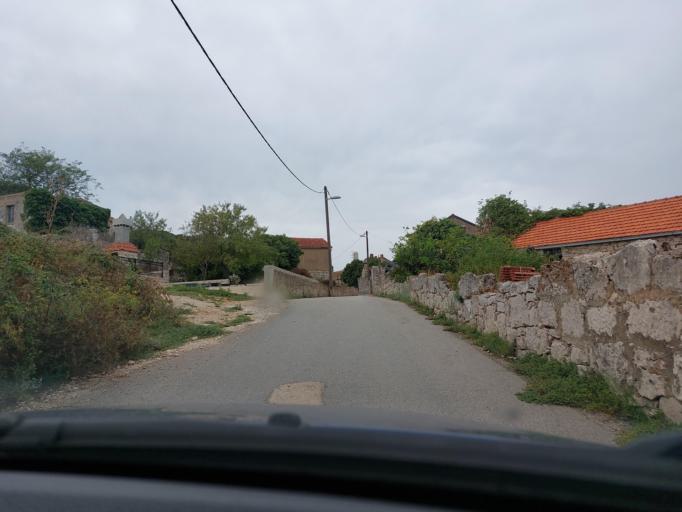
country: HR
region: Dubrovacko-Neretvanska
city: Smokvica
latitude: 42.7654
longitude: 16.9009
